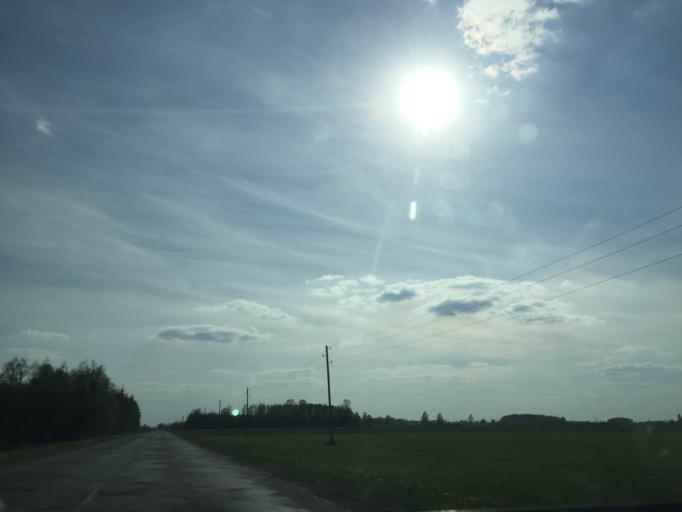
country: LV
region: Bauskas Rajons
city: Bauska
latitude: 56.4580
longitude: 24.2708
